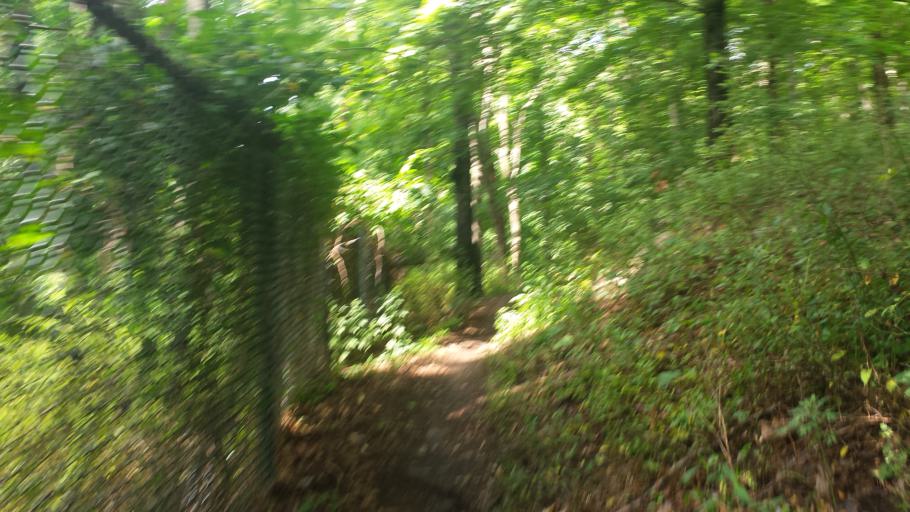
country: US
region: New York
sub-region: Westchester County
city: Hawthorne
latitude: 41.1144
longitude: -73.8038
